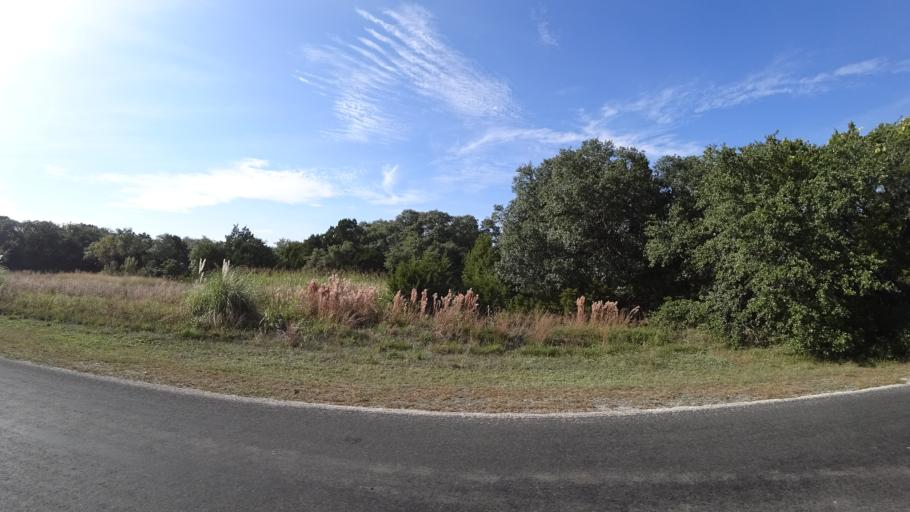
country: US
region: Texas
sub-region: Travis County
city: Bee Cave
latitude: 30.2338
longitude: -97.9340
